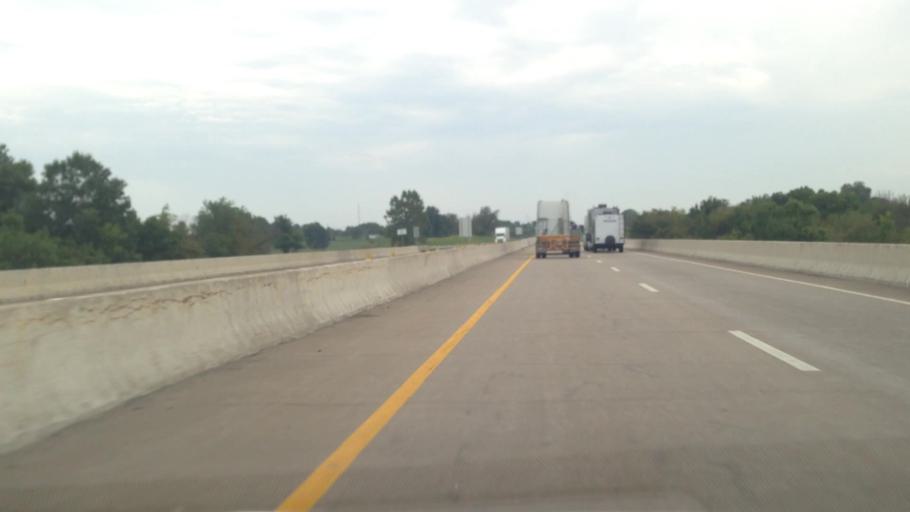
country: US
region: Oklahoma
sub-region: Ottawa County
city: Miami
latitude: 36.8523
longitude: -94.8558
